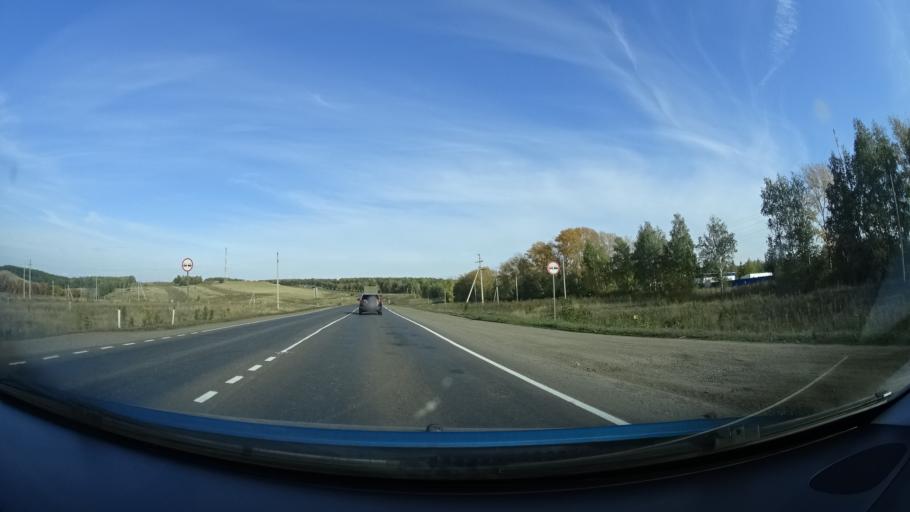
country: RU
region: Bashkortostan
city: Buzdyak
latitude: 54.6768
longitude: 54.7899
